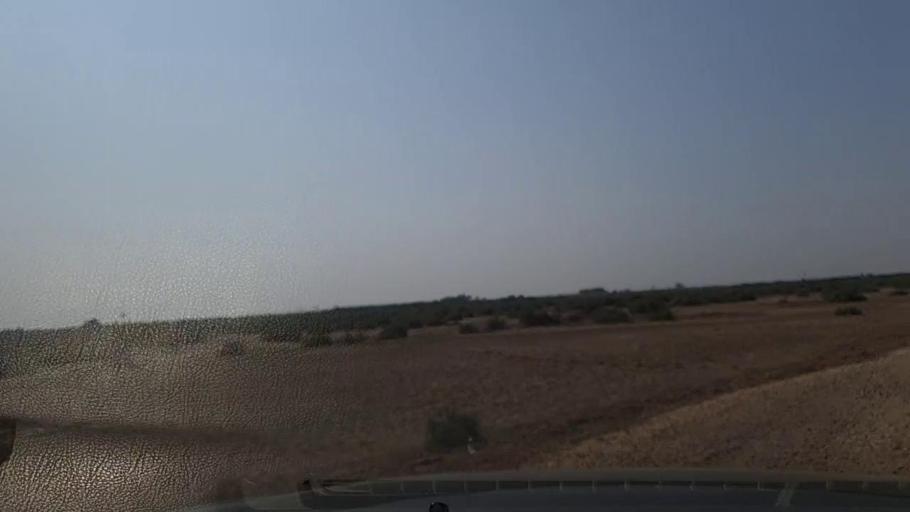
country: PK
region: Sindh
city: Mirpur Sakro
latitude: 24.4266
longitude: 67.7183
